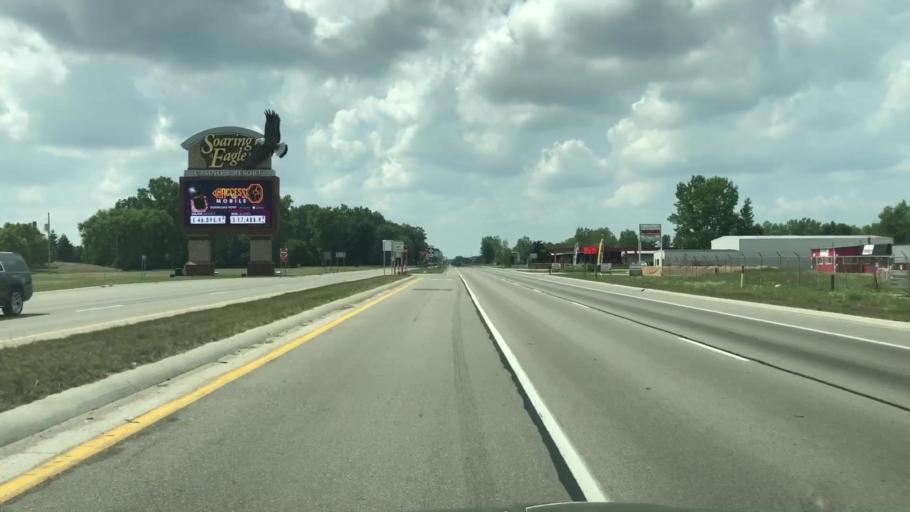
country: US
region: Michigan
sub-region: Isabella County
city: Mount Pleasant
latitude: 43.6117
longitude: -84.7094
